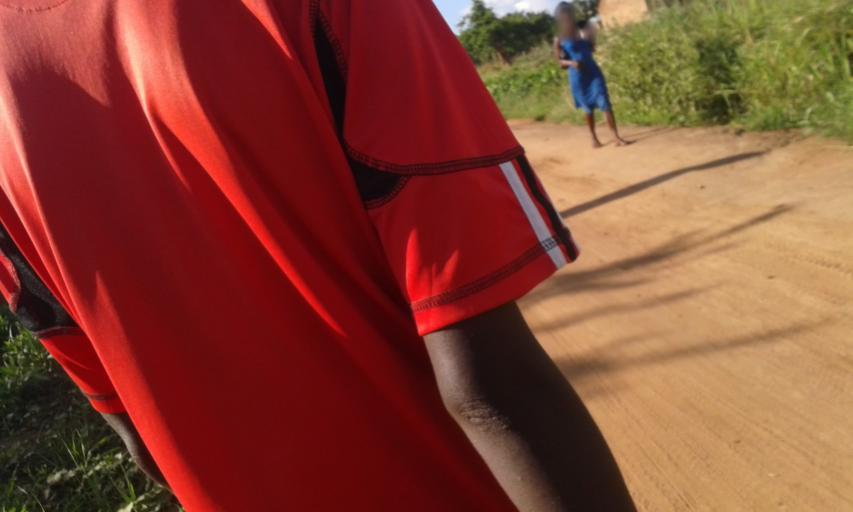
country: UG
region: Northern Region
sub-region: Gulu District
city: Gulu
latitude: 2.8029
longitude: 32.3059
